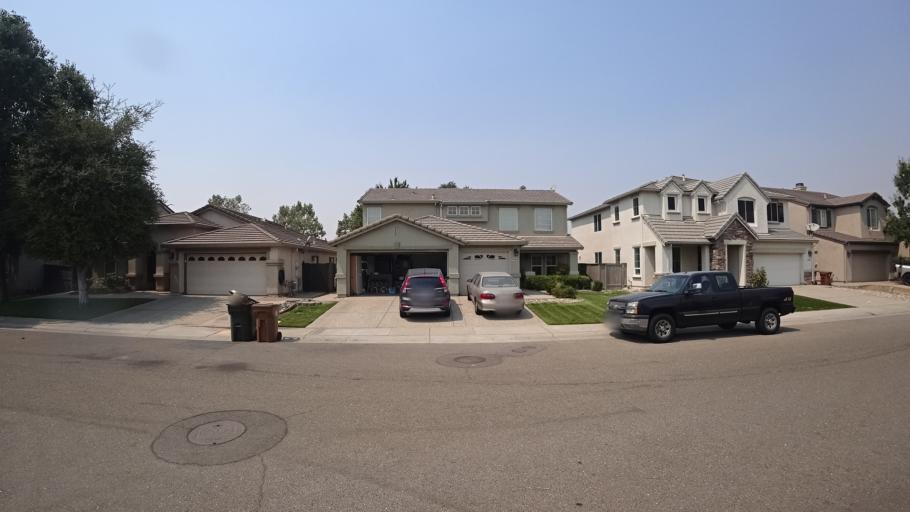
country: US
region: California
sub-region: Sacramento County
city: Laguna
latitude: 38.4032
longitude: -121.4401
